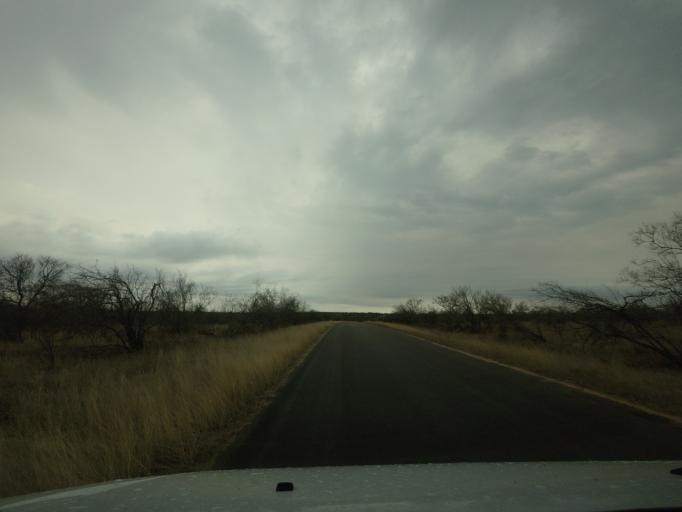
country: ZA
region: Limpopo
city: Thulamahashi
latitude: -24.4687
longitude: 31.4393
